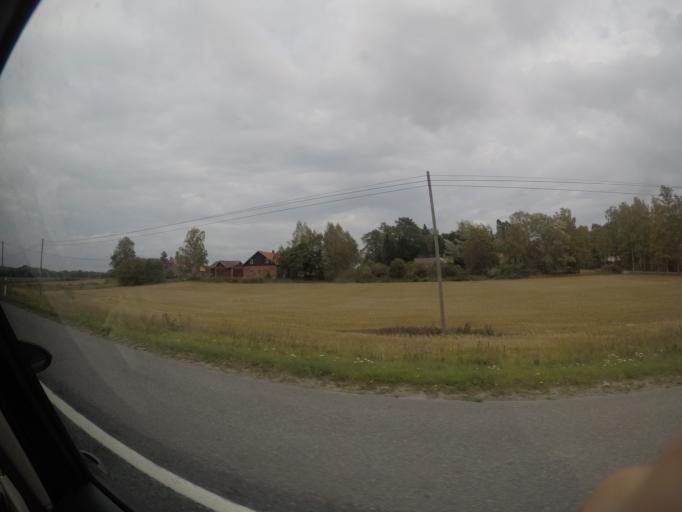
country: FI
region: Haeme
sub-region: Haemeenlinna
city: Haemeenlinna
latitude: 61.0285
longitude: 24.4197
